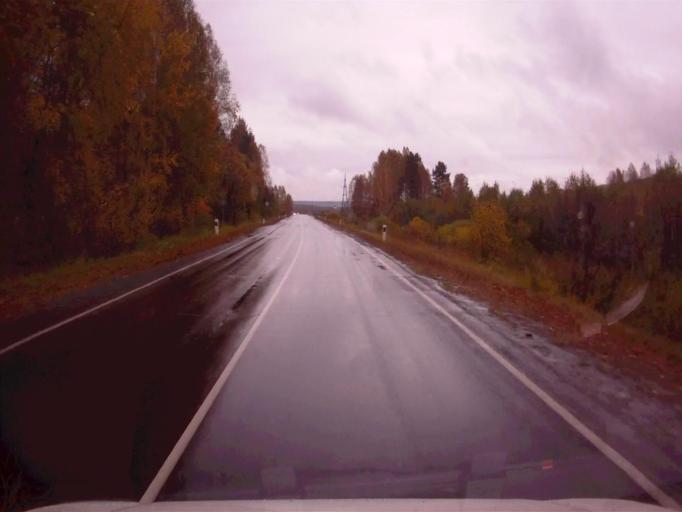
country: RU
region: Chelyabinsk
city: Verkhniy Ufaley
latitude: 55.9959
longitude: 60.3324
